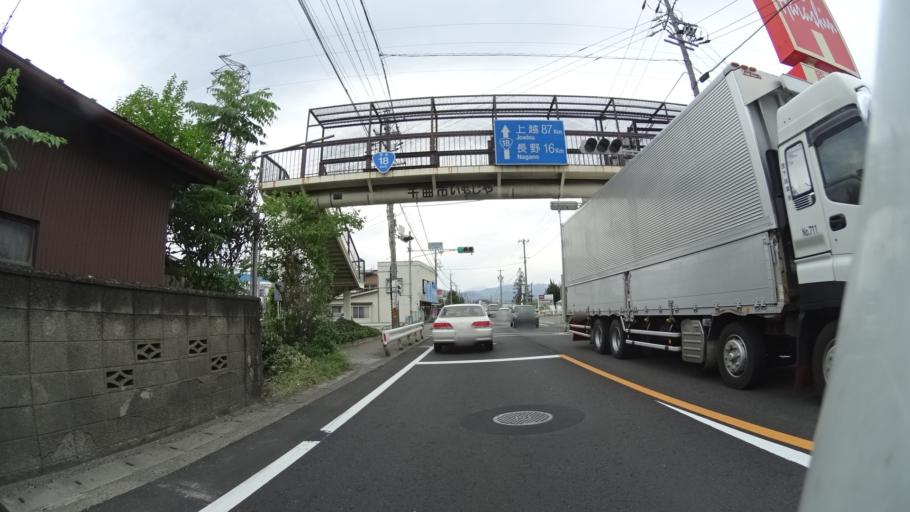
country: JP
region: Nagano
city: Nagano-shi
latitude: 36.5202
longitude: 138.1286
